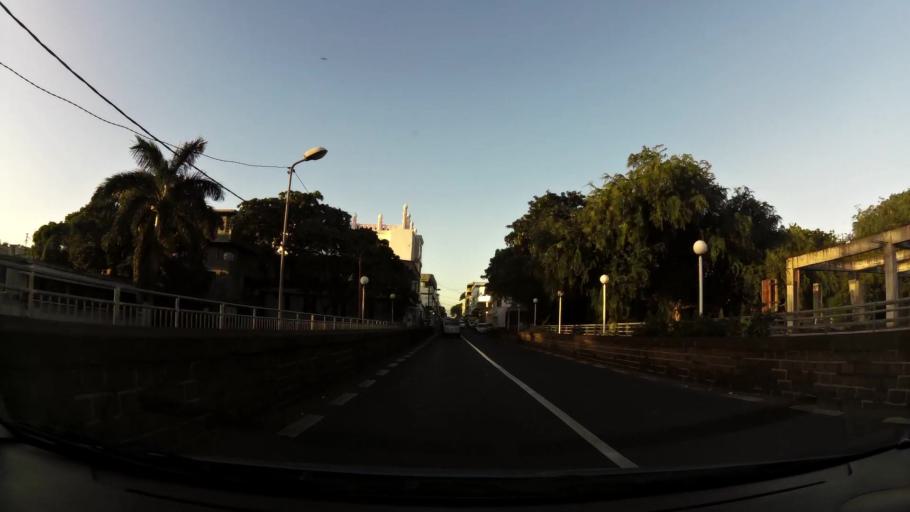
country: MU
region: Port Louis
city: Port Louis
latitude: -20.1560
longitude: 57.5093
